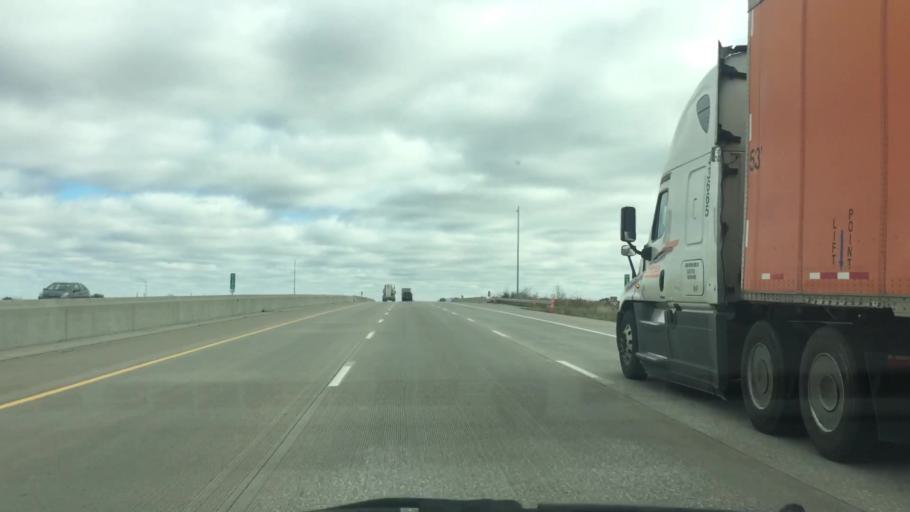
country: US
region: Iowa
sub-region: Polk County
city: Altoona
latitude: 41.6619
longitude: -93.4971
